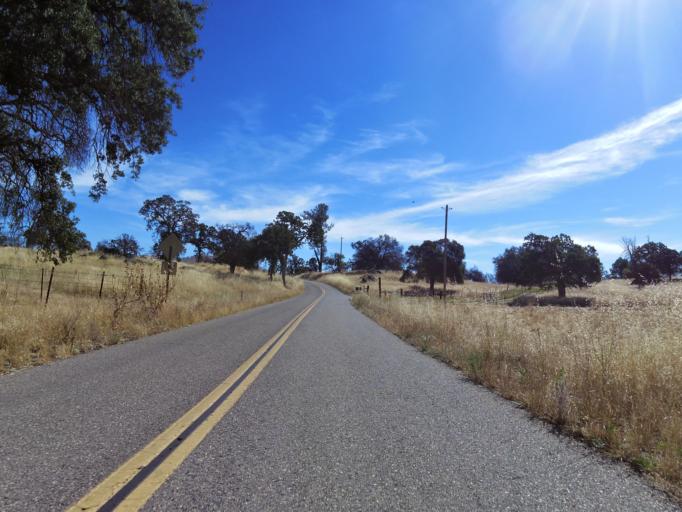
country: US
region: California
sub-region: Mariposa County
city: Mariposa
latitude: 37.3073
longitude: -119.9725
